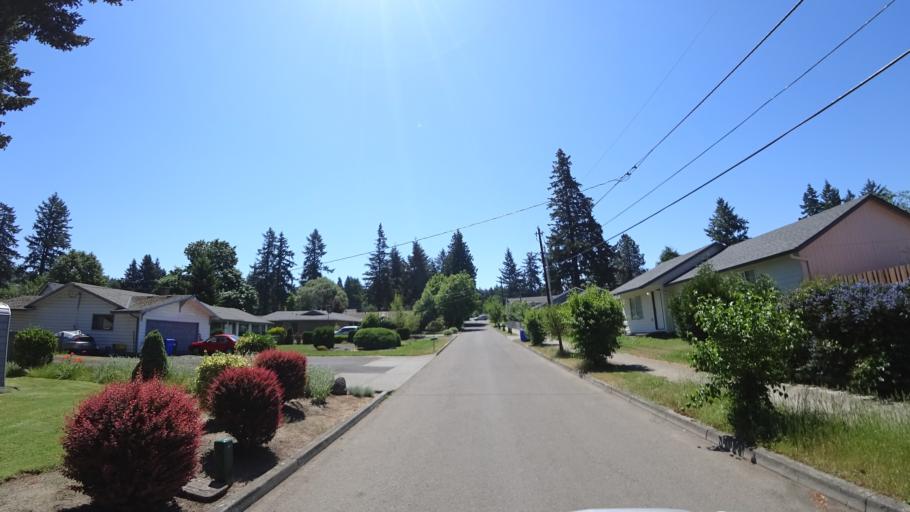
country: US
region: Oregon
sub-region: Clackamas County
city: Happy Valley
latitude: 45.4781
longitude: -122.5200
